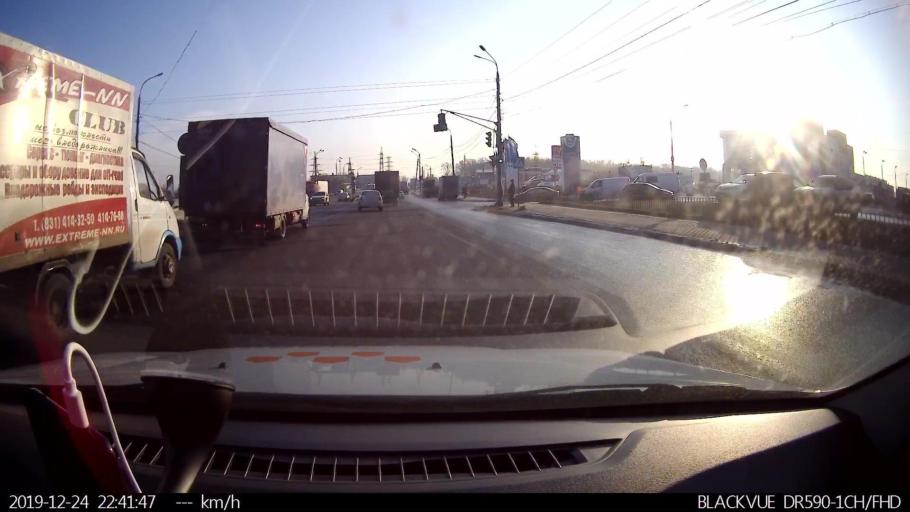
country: RU
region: Nizjnij Novgorod
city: Nizhniy Novgorod
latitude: 56.2910
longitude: 43.8832
